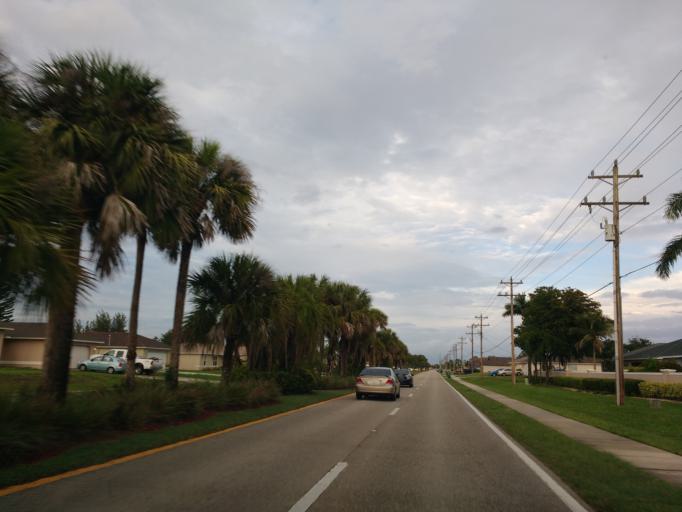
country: US
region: Florida
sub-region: Lee County
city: Cape Coral
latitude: 26.6229
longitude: -81.9831
